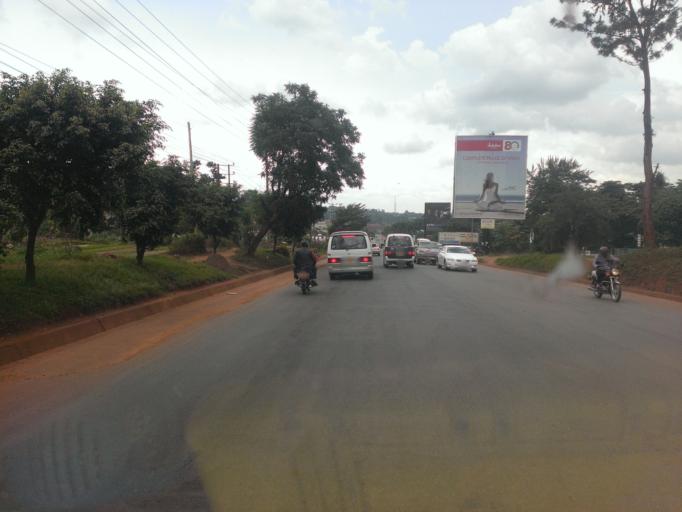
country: UG
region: Central Region
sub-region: Wakiso District
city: Kireka
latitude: 0.3325
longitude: 32.6165
